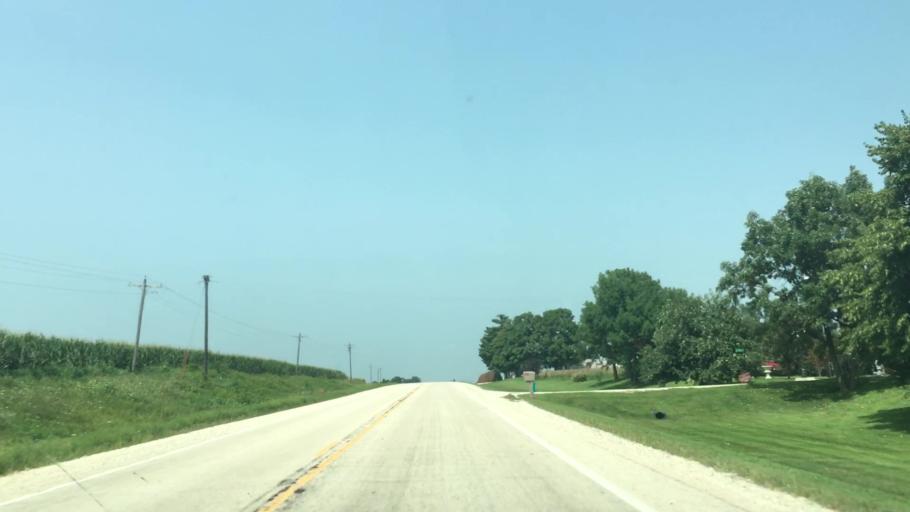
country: US
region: Iowa
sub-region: Fayette County
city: West Union
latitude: 43.0064
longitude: -91.8243
